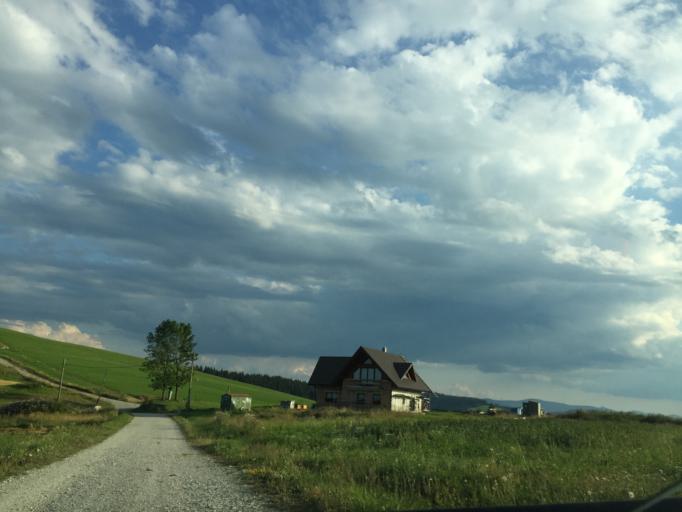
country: PL
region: Silesian Voivodeship
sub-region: Powiat zywiecki
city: Korbielow
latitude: 49.4571
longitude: 19.3183
